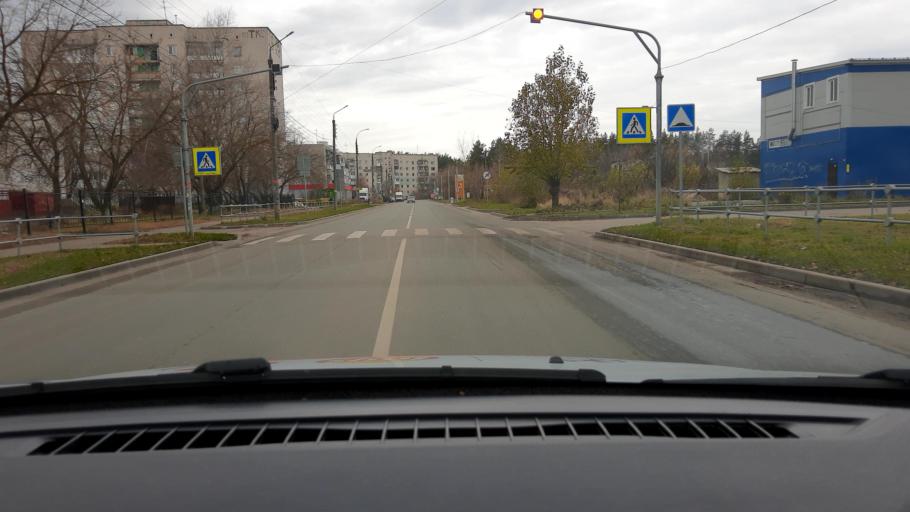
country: RU
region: Nizjnij Novgorod
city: Dzerzhinsk
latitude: 56.2562
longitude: 43.4589
